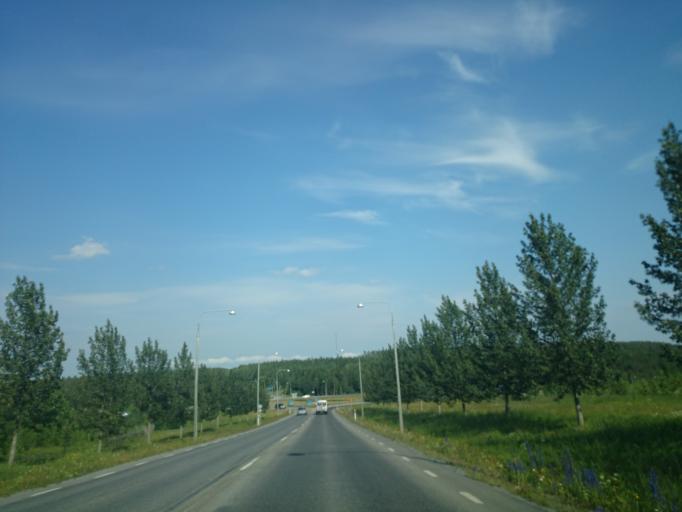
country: SE
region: Jaemtland
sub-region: OEstersunds Kommun
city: Ostersund
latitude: 63.1794
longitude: 14.6856
